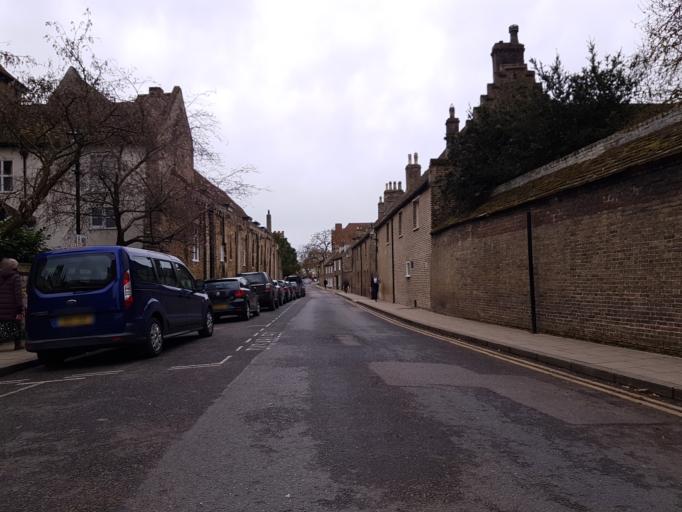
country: GB
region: England
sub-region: Cambridgeshire
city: Ely
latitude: 52.3981
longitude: 0.2622
